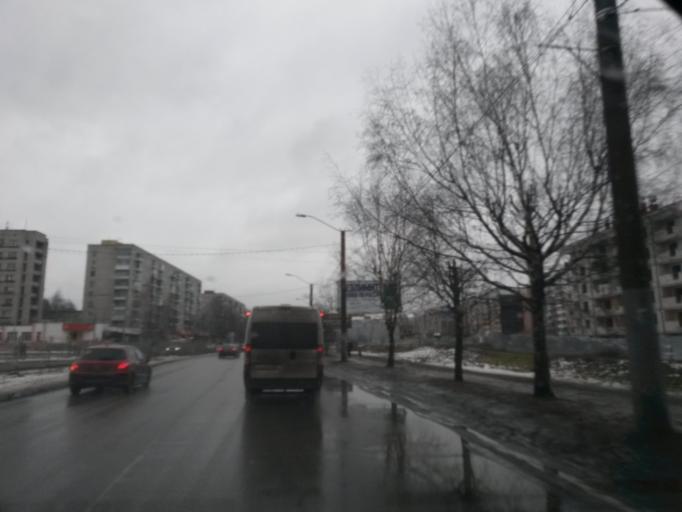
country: RU
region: Jaroslavl
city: Yaroslavl
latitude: 57.6459
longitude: 39.9545
